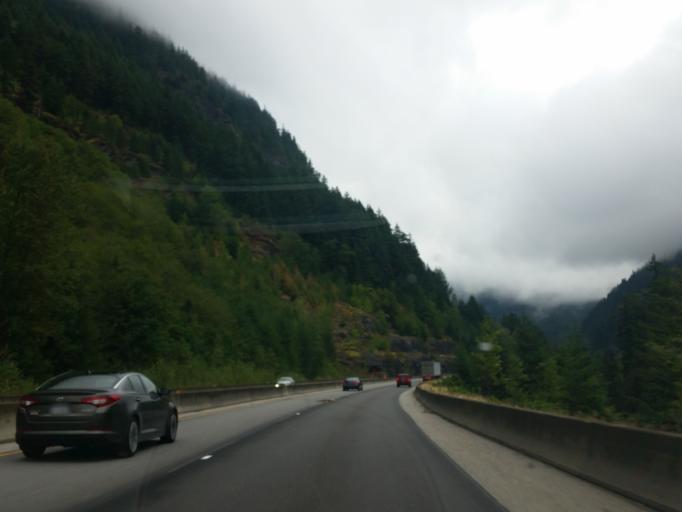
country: CA
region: British Columbia
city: Hope
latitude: 49.4393
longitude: -121.3010
